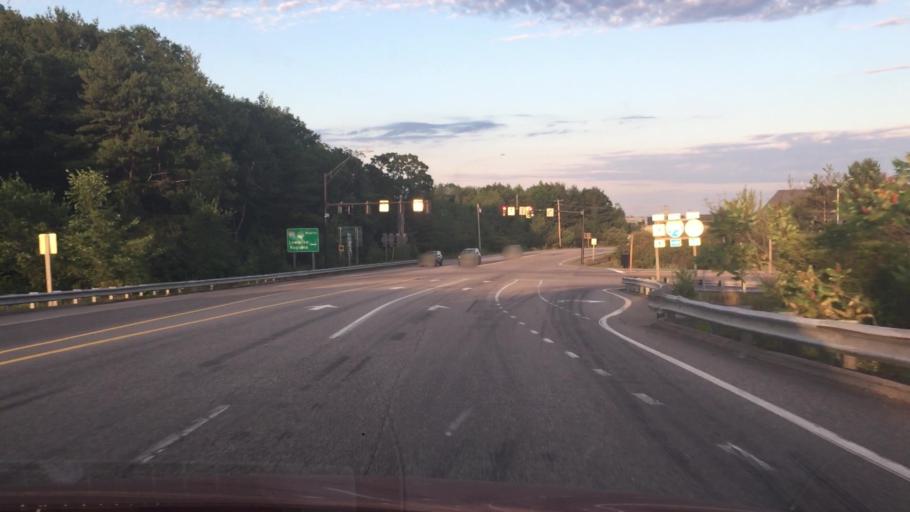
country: US
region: Maine
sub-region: Cumberland County
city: South Portland Gardens
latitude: 43.6494
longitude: -70.3299
